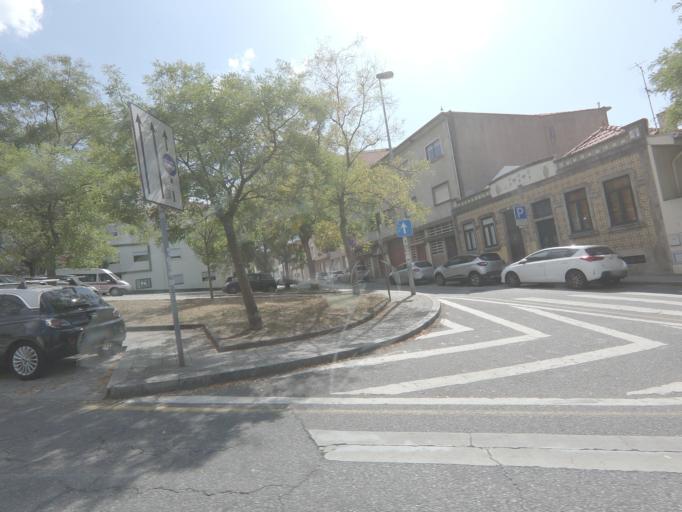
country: PT
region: Porto
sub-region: Porto
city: Porto
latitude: 41.1632
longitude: -8.6238
